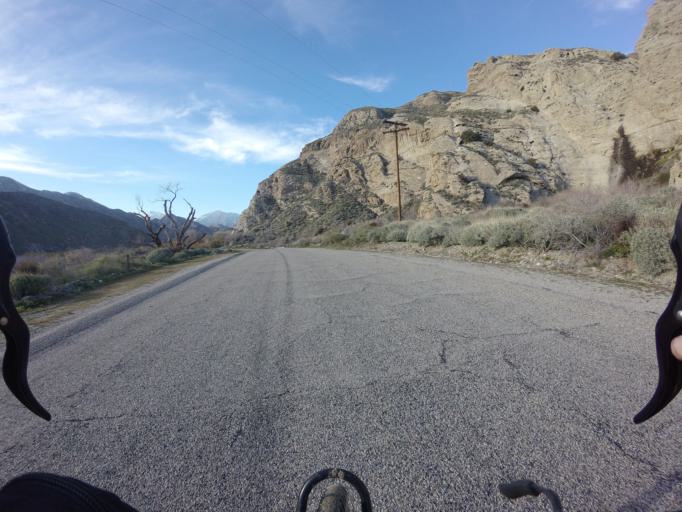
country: US
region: California
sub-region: San Bernardino County
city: Morongo Valley
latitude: 33.9845
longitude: -116.6523
